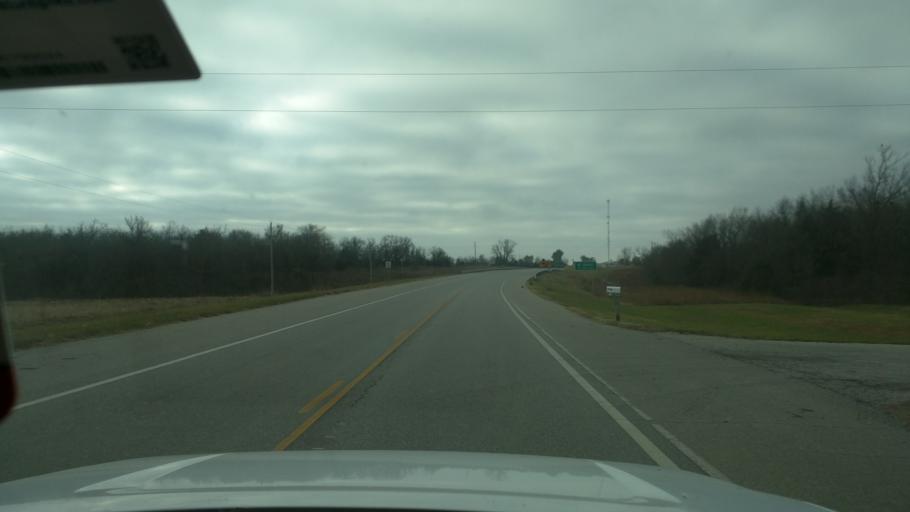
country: US
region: Kansas
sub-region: Elk County
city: Howard
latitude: 37.6398
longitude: -96.2342
